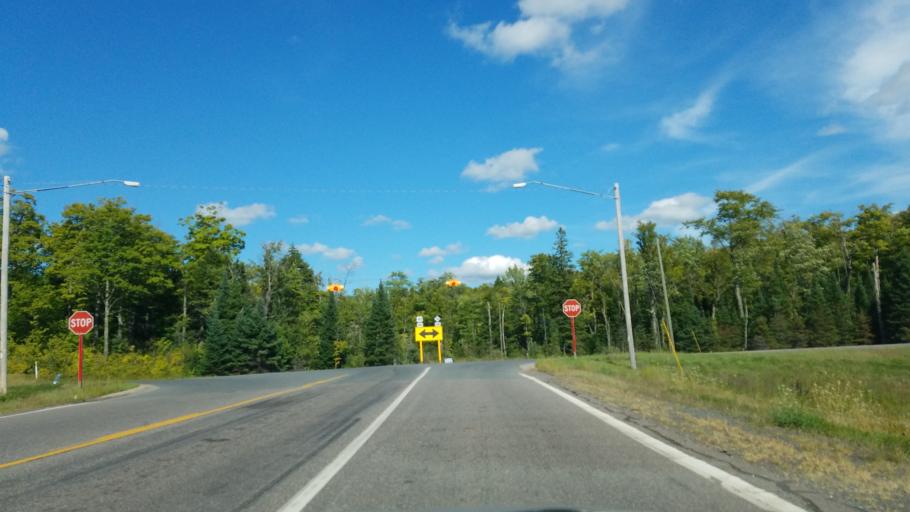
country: US
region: Michigan
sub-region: Baraga County
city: L'Anse
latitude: 46.5850
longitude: -88.4729
